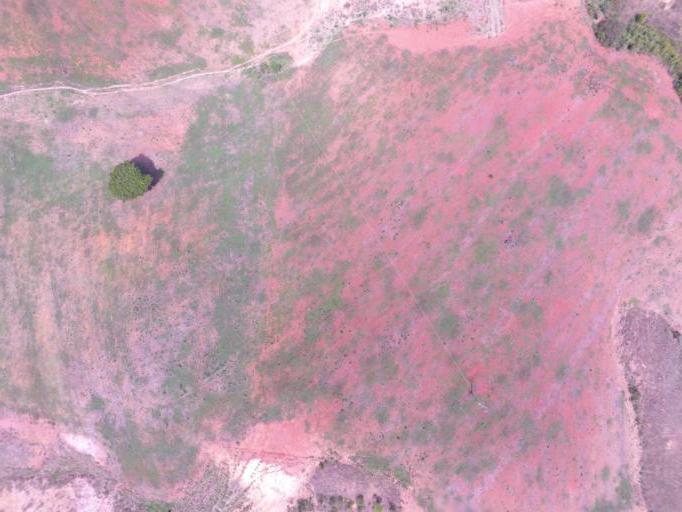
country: BR
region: Minas Gerais
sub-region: Barroso
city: Barroso
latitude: -21.0386
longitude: -44.0036
